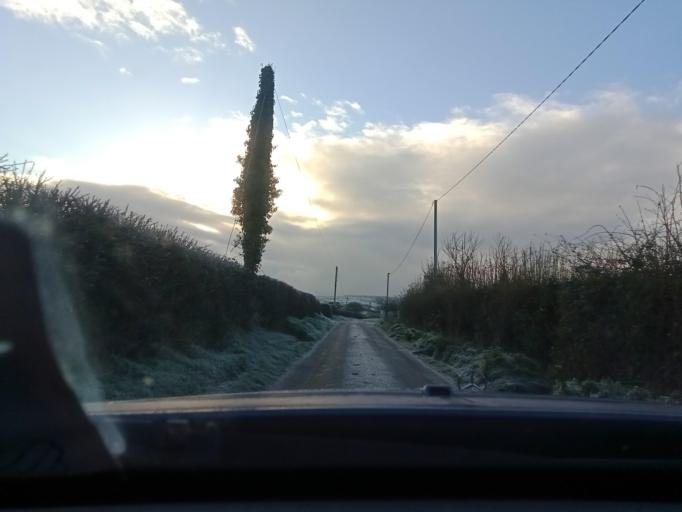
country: IE
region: Leinster
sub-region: County Carlow
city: Bagenalstown
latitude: 52.6337
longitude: -7.0155
